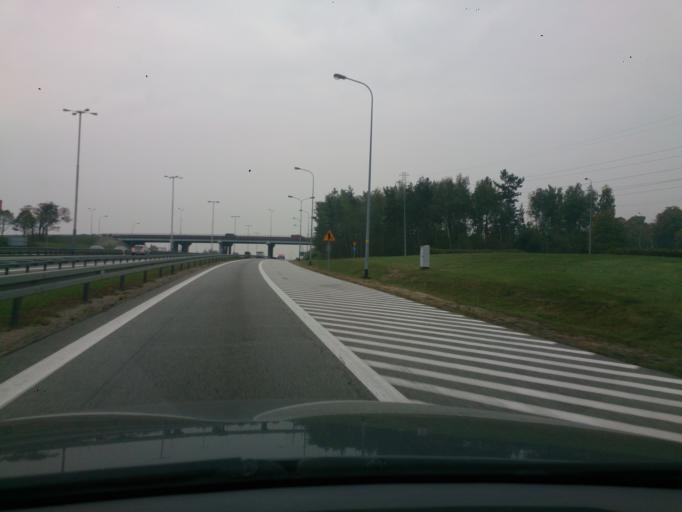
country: PL
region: Pomeranian Voivodeship
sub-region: Sopot
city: Sopot
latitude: 54.3779
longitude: 18.5124
